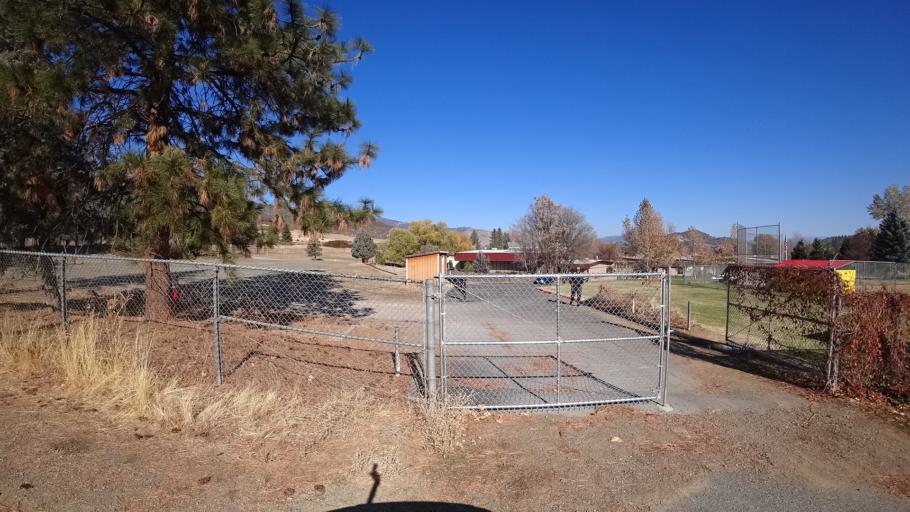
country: US
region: California
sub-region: Siskiyou County
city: Yreka
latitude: 41.7402
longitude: -122.6393
